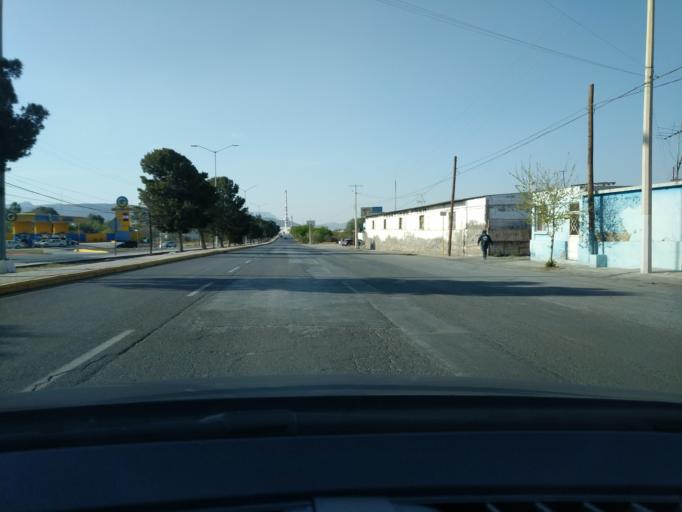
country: MX
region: Coahuila
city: Saltillo
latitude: 25.4733
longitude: -100.9824
